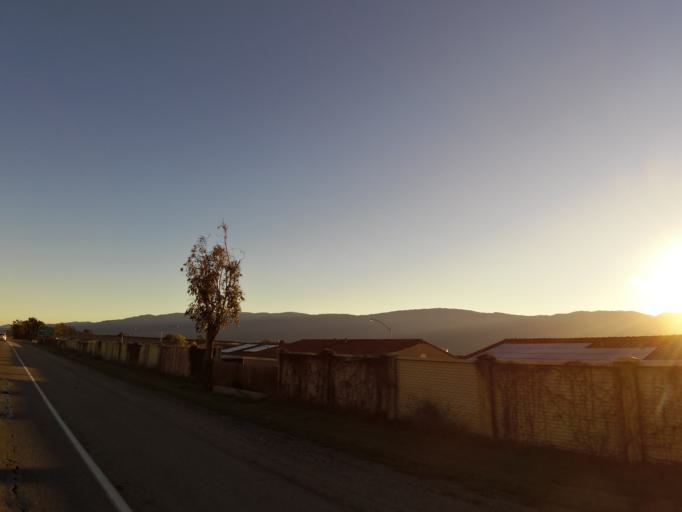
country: US
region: California
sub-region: Monterey County
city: Gonzales
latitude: 36.5066
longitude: -121.4344
